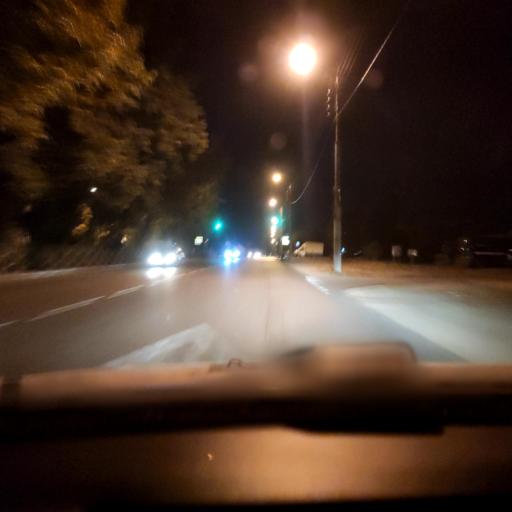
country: RU
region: Voronezj
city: Voronezh
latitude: 51.6292
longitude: 39.1755
